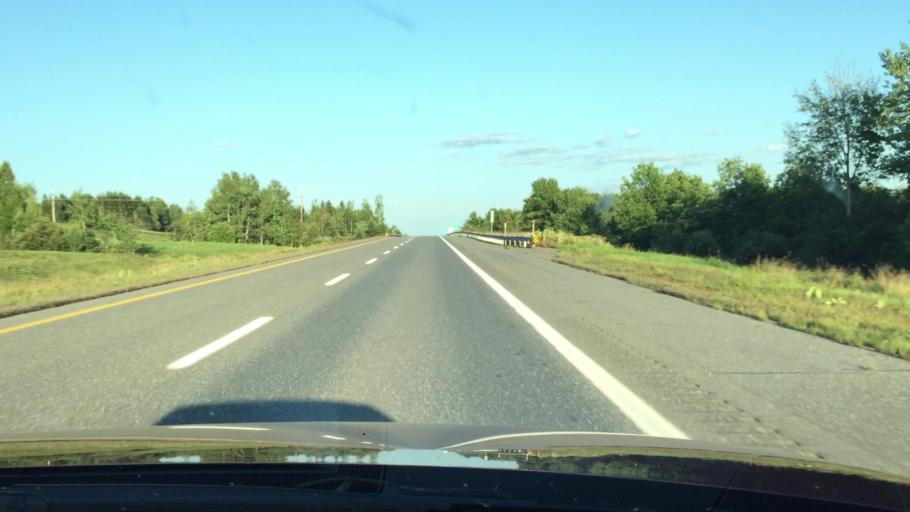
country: US
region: Maine
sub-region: Aroostook County
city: Hodgdon
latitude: 46.1435
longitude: -68.0443
